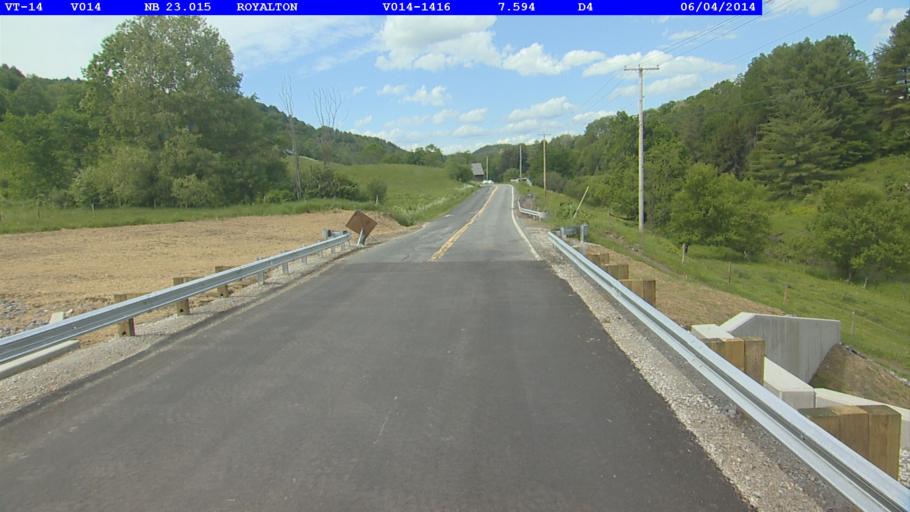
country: US
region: Vermont
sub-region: Orange County
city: Randolph
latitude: 43.8447
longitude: -72.5869
